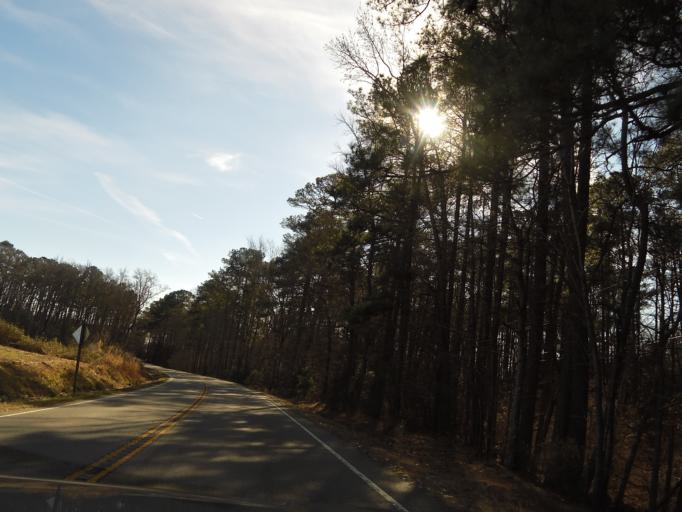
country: US
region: Virginia
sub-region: Isle of Wight County
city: Windsor
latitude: 36.8528
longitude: -76.7539
